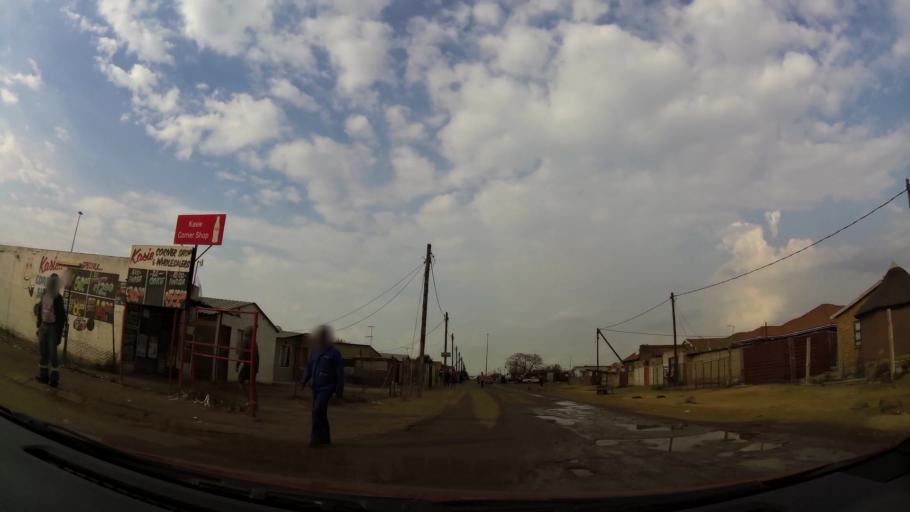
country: ZA
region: Gauteng
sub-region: Sedibeng District Municipality
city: Vanderbijlpark
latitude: -26.6760
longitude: 27.8644
